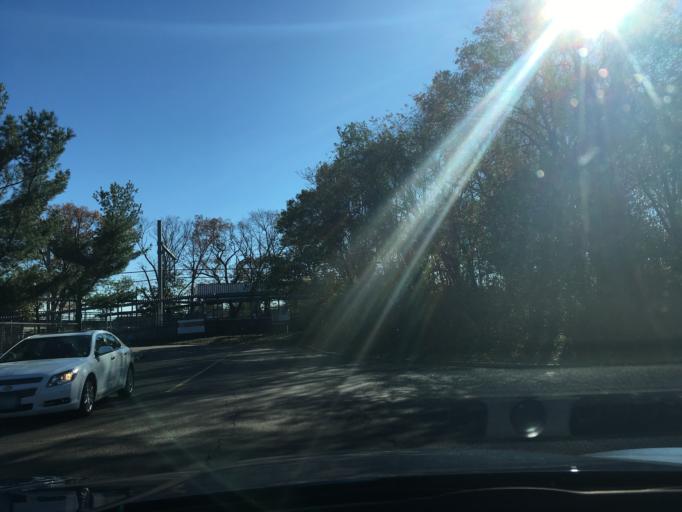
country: US
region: Massachusetts
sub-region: Bristol County
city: North Seekonk
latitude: 41.8982
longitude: -71.3565
